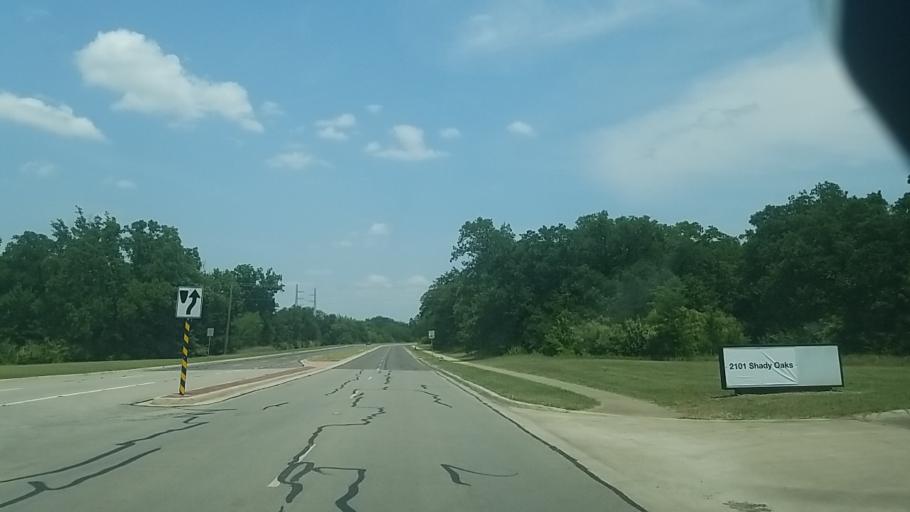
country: US
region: Texas
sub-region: Denton County
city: Denton
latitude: 33.2044
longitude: -97.1064
